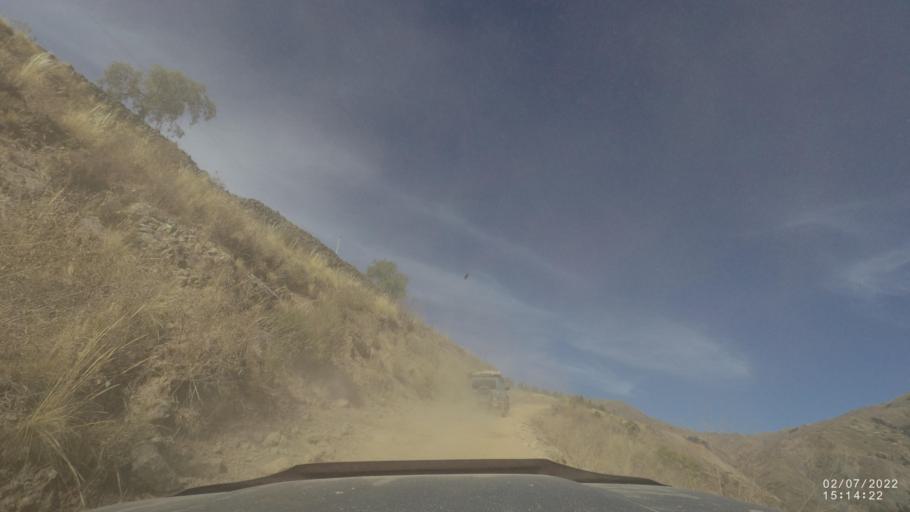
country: BO
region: Cochabamba
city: Irpa Irpa
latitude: -17.8621
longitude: -66.4368
